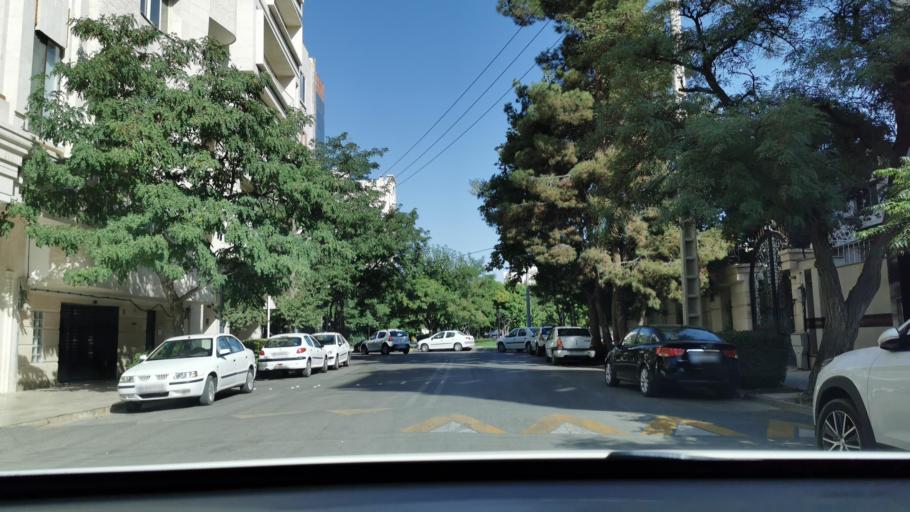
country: IR
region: Razavi Khorasan
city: Mashhad
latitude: 36.3152
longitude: 59.5474
